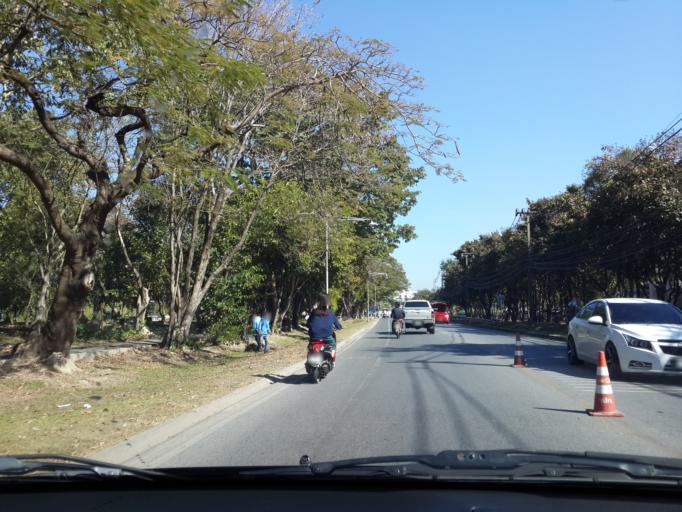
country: TH
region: Chiang Mai
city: Chiang Mai
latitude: 18.7960
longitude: 98.9575
